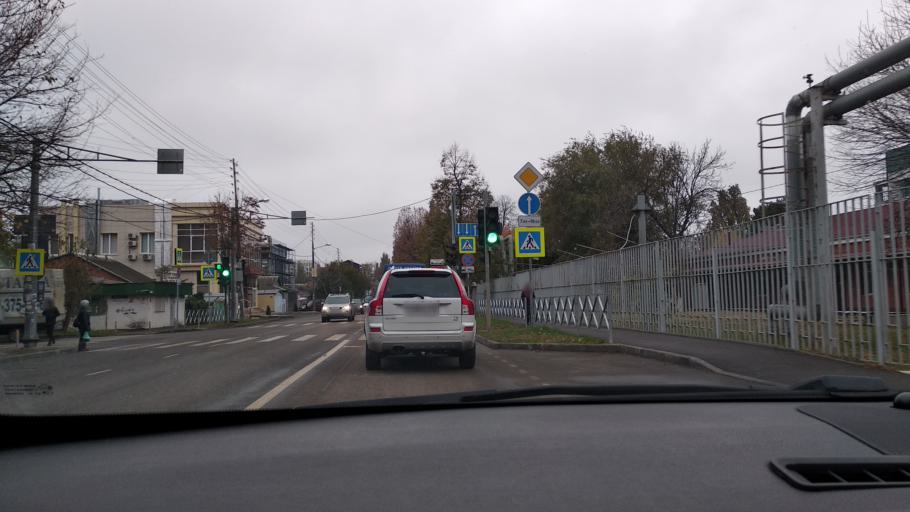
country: RU
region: Krasnodarskiy
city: Krasnodar
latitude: 45.0414
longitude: 38.9855
